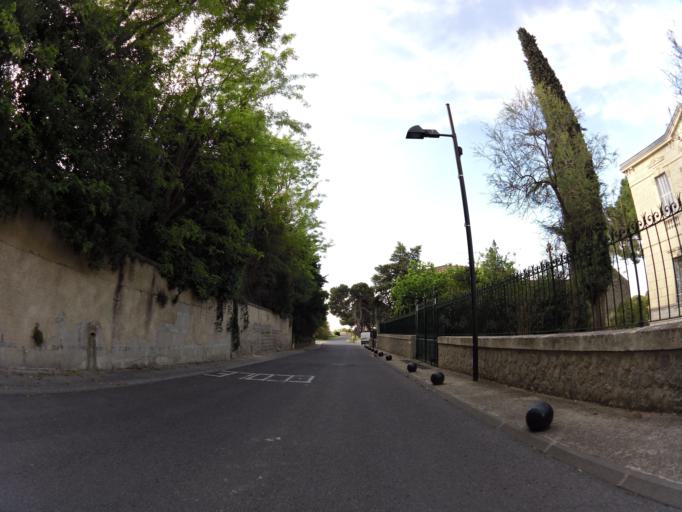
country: FR
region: Languedoc-Roussillon
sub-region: Departement du Gard
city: Gallargues-le-Montueux
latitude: 43.7191
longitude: 4.1743
